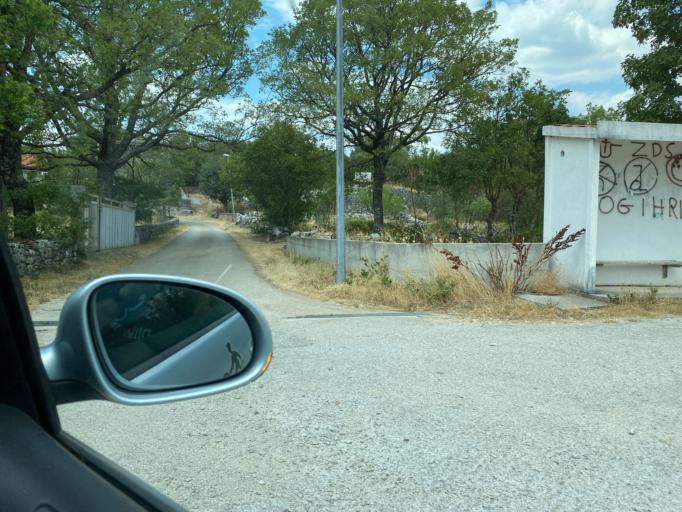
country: HR
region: Splitsko-Dalmatinska
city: Hrvace
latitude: 43.8046
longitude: 16.6230
